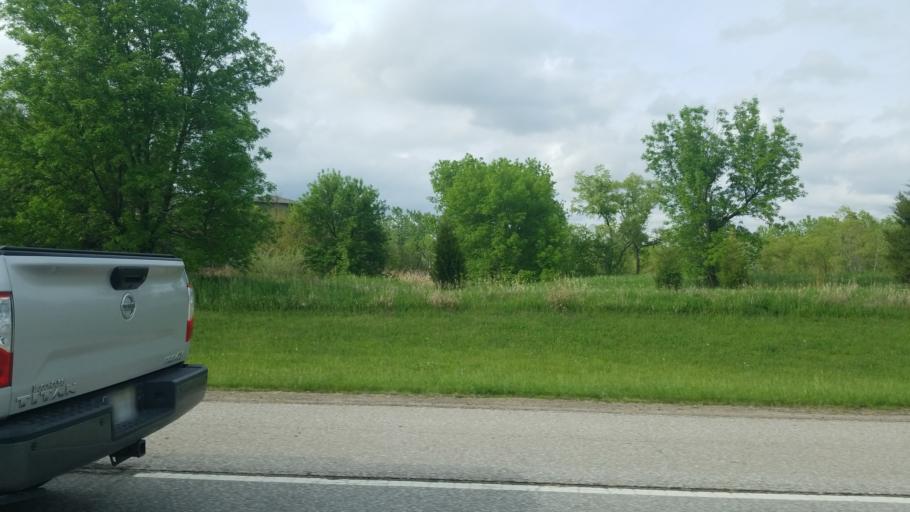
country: US
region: Nebraska
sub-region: Lancaster County
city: Lincoln
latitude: 40.8750
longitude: -96.7313
